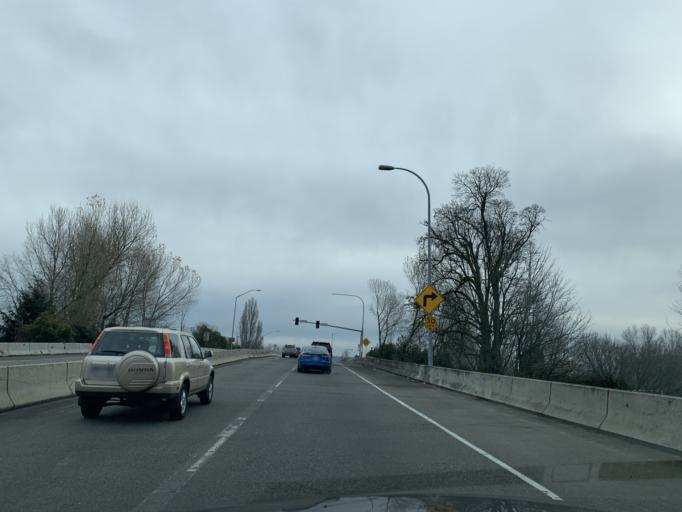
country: US
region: Washington
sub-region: King County
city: Tukwila
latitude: 47.4649
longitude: -122.2488
